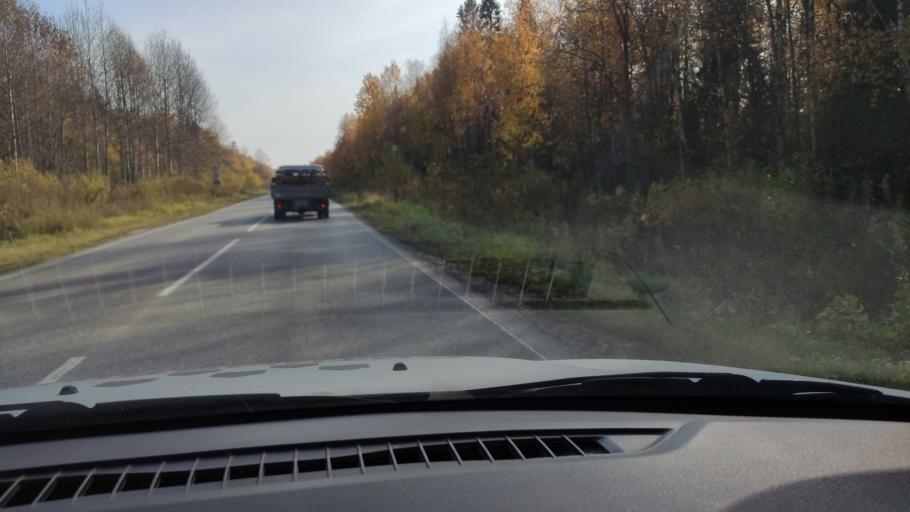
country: RU
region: Perm
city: Novyye Lyady
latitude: 58.0259
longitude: 56.6324
